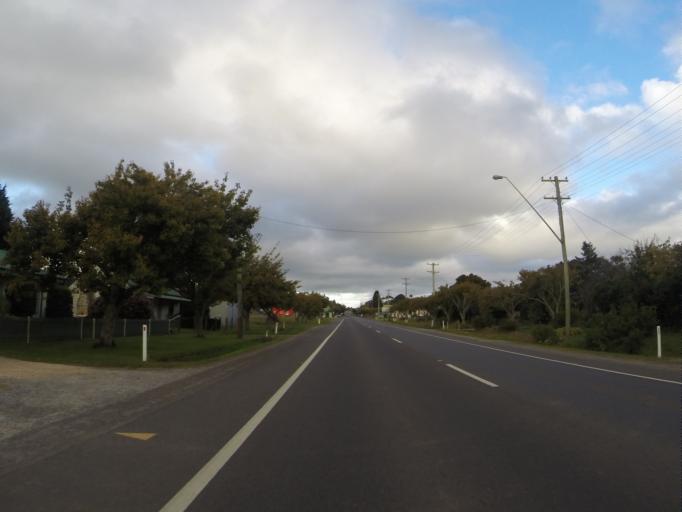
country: AU
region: New South Wales
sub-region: Shellharbour
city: Calderwood
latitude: -34.5879
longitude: 150.5872
